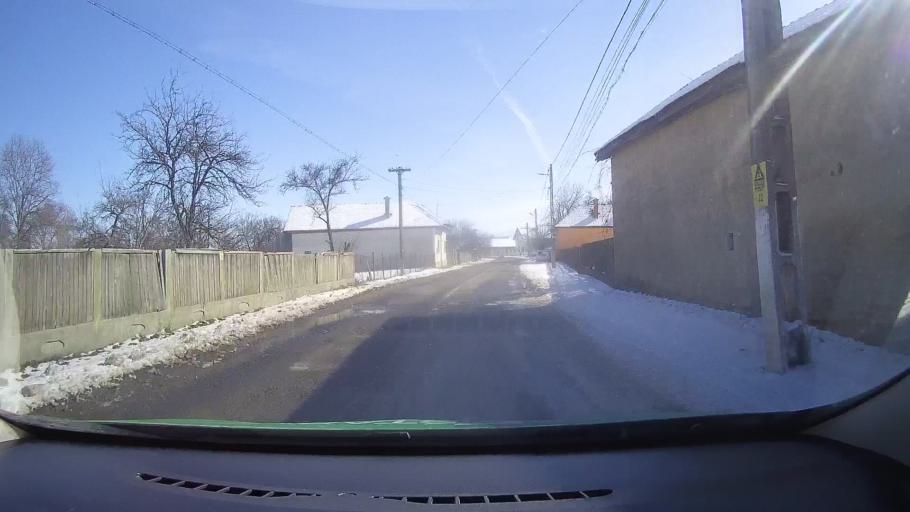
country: RO
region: Brasov
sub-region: Comuna Recea
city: Recea
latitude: 45.7313
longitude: 24.9474
